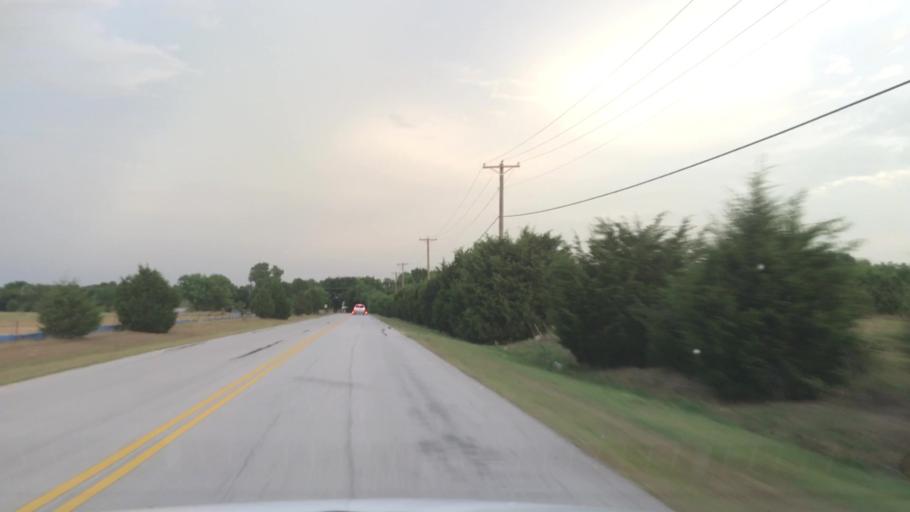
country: US
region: Texas
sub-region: Dallas County
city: Seagoville
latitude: 32.6953
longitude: -96.5563
